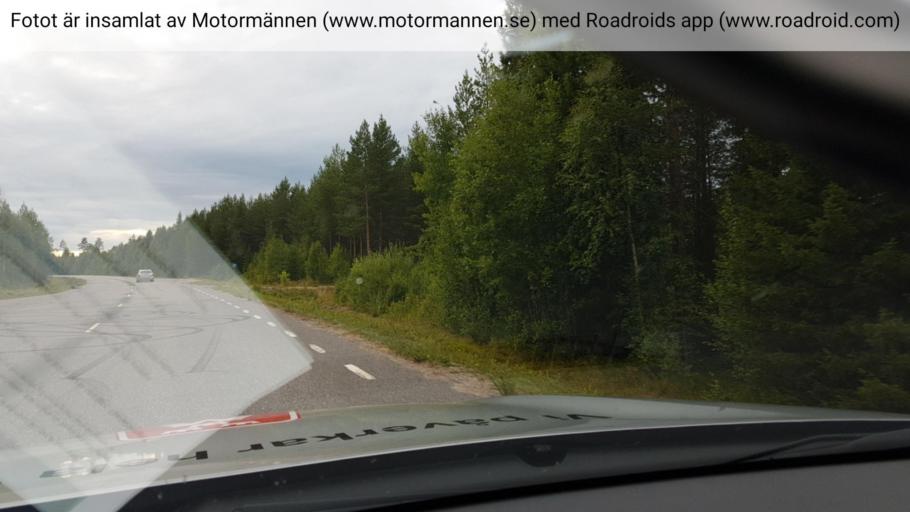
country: SE
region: Norrbotten
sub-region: Lulea Kommun
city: Gammelstad
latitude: 65.6635
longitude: 22.0785
